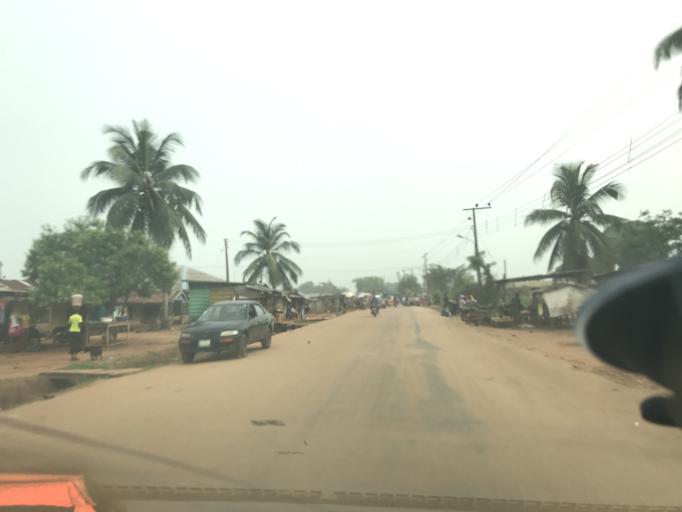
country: NG
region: Ogun
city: Ado Odo
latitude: 6.5089
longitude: 2.9539
